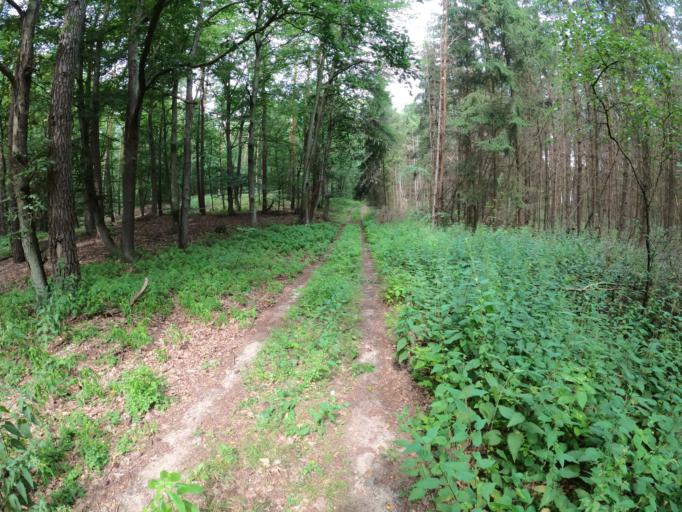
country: DE
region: Brandenburg
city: Angermunde
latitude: 53.0352
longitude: 13.9403
